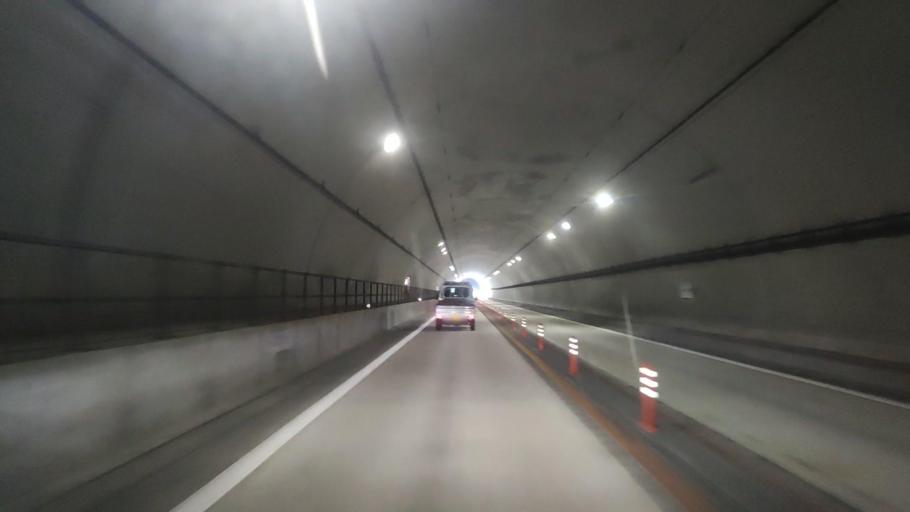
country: JP
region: Wakayama
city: Tanabe
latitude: 33.6107
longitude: 135.4259
